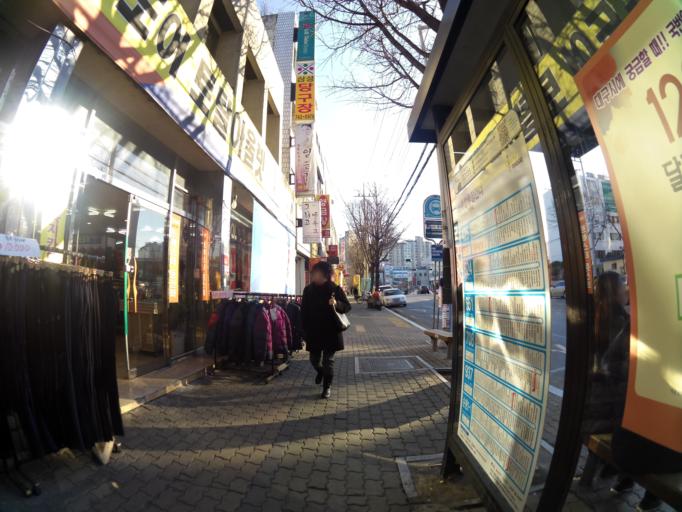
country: KR
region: Daegu
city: Daegu
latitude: 35.8741
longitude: 128.6346
